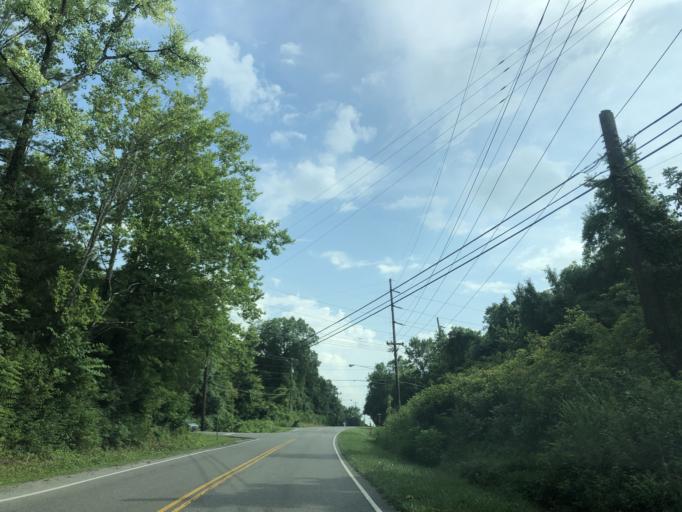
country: US
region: Tennessee
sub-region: Davidson County
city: Oak Hill
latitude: 36.0991
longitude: -86.6726
